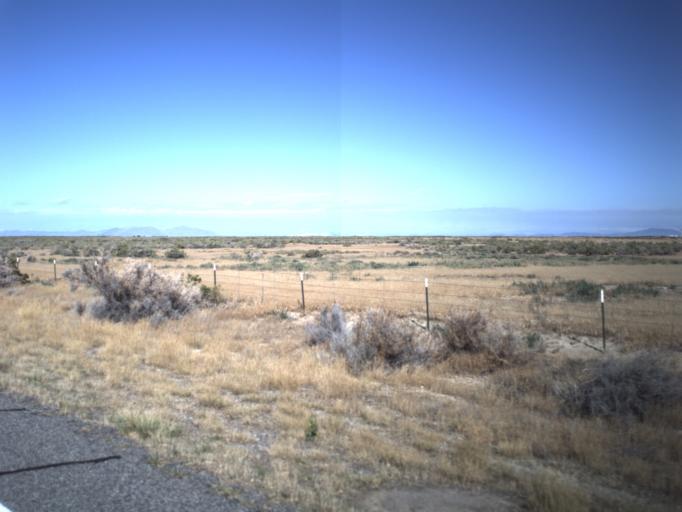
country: US
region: Utah
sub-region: Millard County
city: Delta
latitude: 39.3538
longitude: -112.4477
